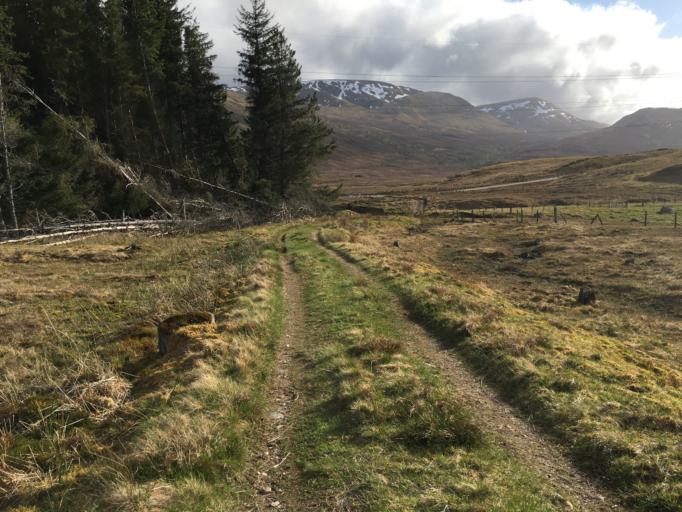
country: GB
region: Scotland
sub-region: Highland
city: Kingussie
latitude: 57.0253
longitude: -4.4325
